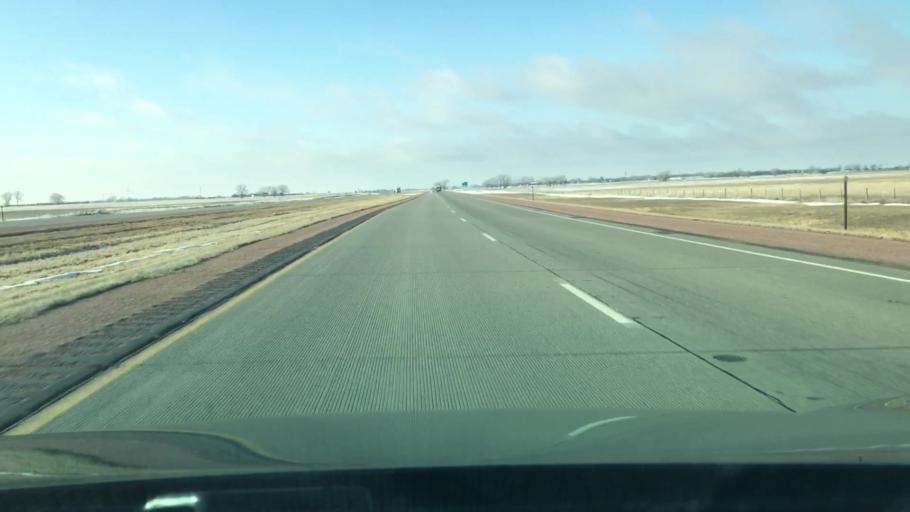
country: US
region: South Dakota
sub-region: Aurora County
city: Plankinton
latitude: 43.7120
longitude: -98.6786
